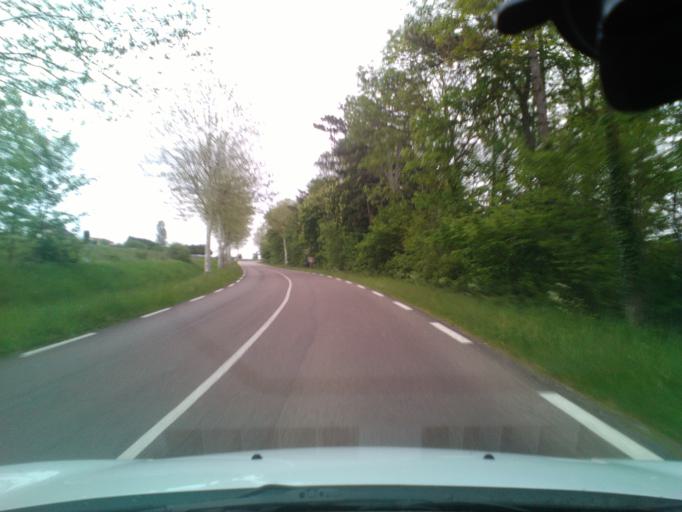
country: FR
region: Champagne-Ardenne
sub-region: Departement de l'Aube
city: Bar-sur-Aube
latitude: 48.2252
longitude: 4.7986
